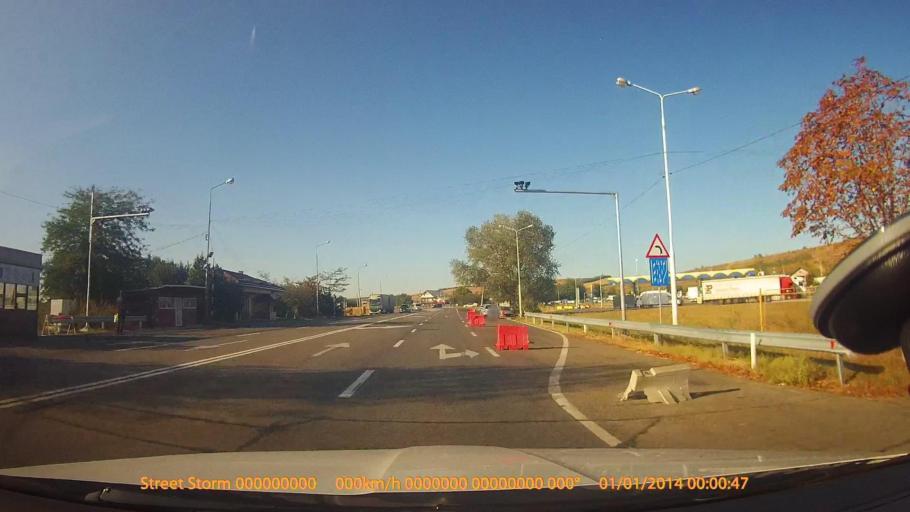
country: RO
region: Vaslui
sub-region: Comuna Dranceni
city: Rasesti
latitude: 46.7848
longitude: 28.1365
